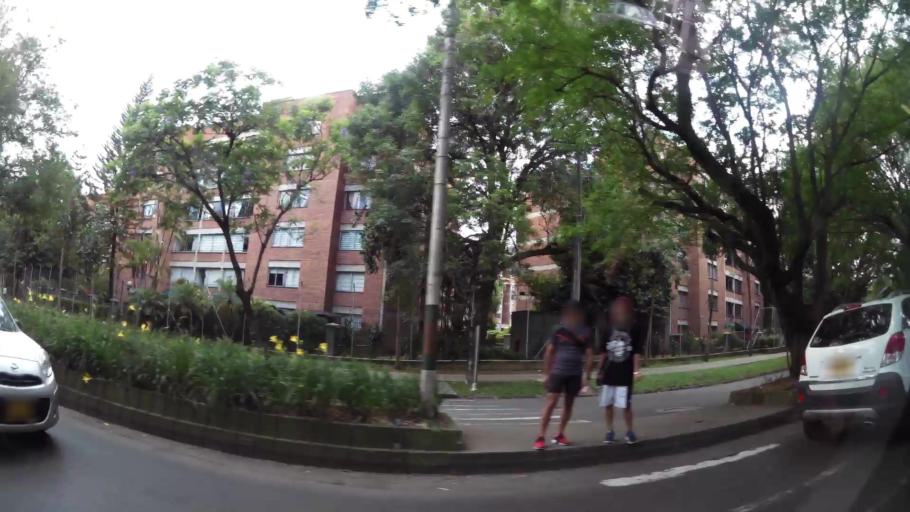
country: CO
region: Antioquia
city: Envigado
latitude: 6.1812
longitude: -75.5826
